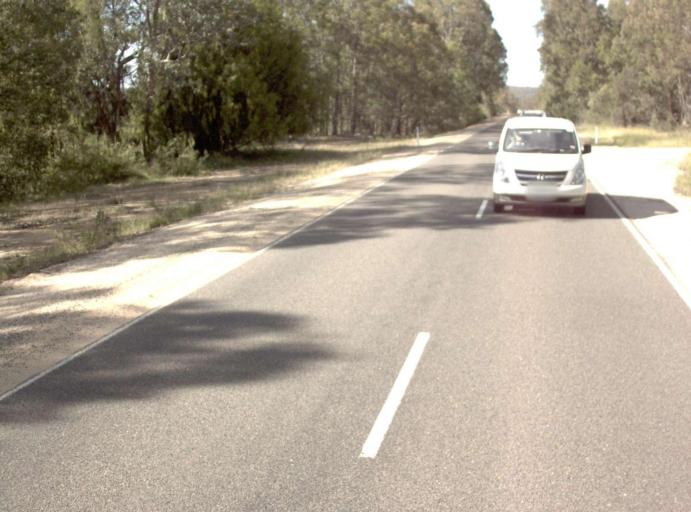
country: AU
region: Victoria
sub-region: East Gippsland
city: Lakes Entrance
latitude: -37.5885
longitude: 148.1229
